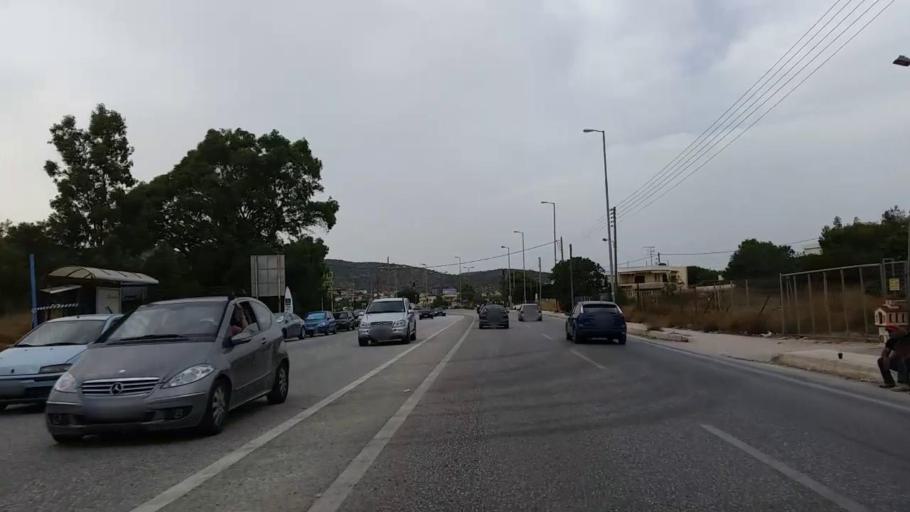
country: GR
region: Attica
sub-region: Nomarchia Anatolikis Attikis
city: Agia Marina
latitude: 37.8147
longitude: 23.8440
